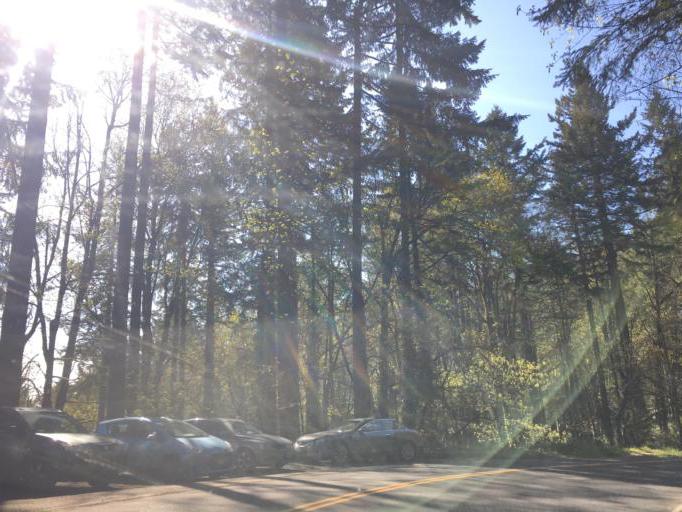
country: US
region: Oregon
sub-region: Multnomah County
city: Portland
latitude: 45.5174
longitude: -122.7074
